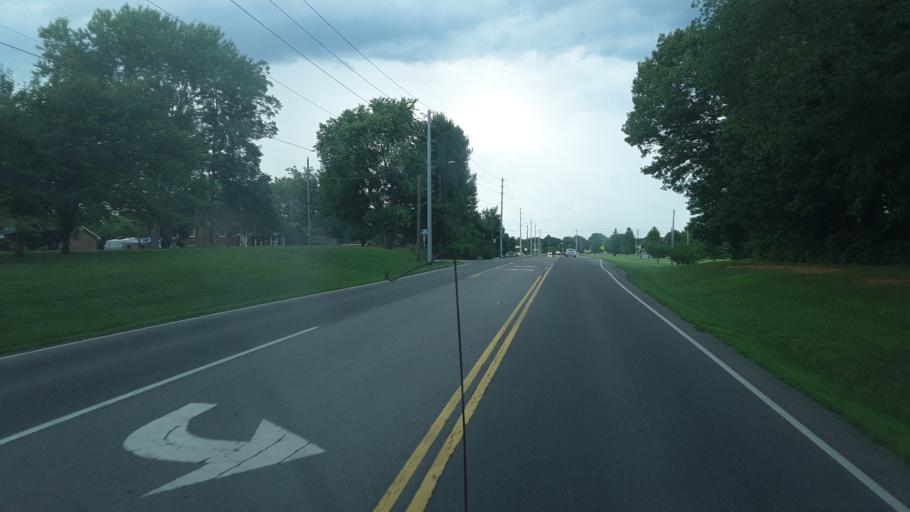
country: US
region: Tennessee
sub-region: Montgomery County
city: Clarksville
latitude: 36.5177
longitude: -87.2783
